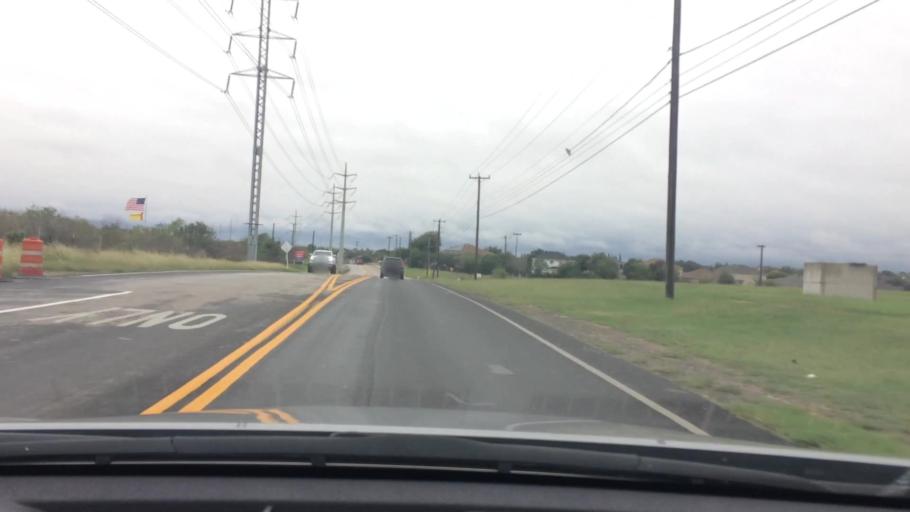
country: US
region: Texas
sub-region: Bexar County
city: Kirby
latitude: 29.4677
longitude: -98.3413
